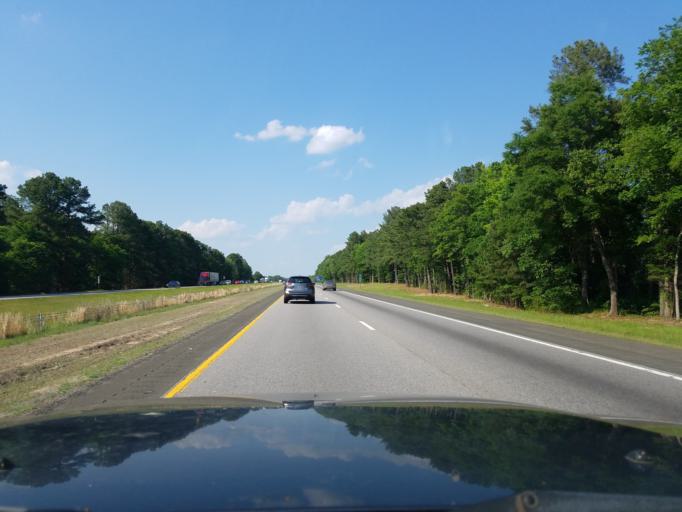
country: US
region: North Carolina
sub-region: Granville County
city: Butner
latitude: 36.1107
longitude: -78.7508
